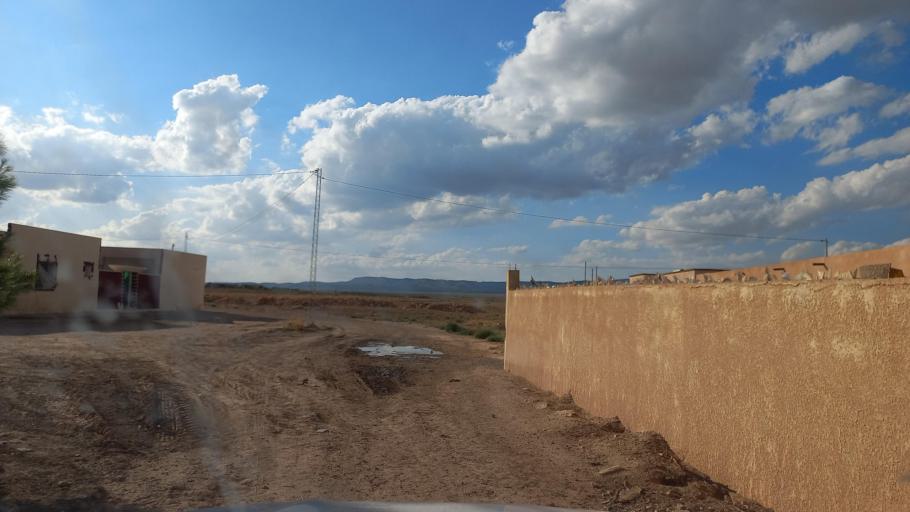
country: TN
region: Al Qasrayn
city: Sbiba
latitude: 35.3885
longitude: 9.0668
